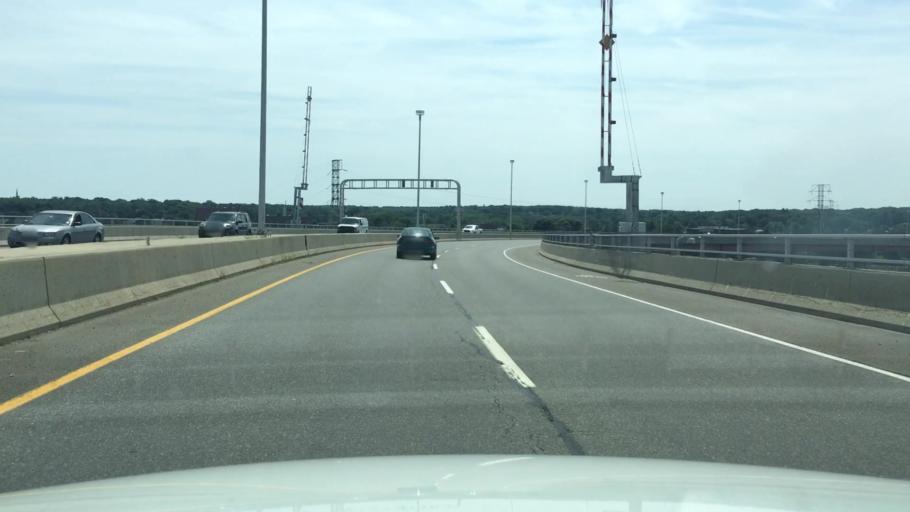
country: US
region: Maine
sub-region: Cumberland County
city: South Portland
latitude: 43.6444
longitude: -70.2574
